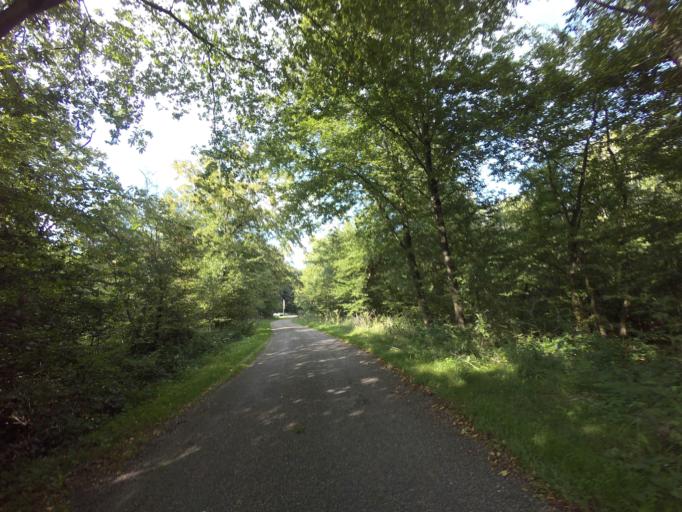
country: NL
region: Flevoland
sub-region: Gemeente Noordoostpolder
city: Ens
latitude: 52.6469
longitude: 5.7727
